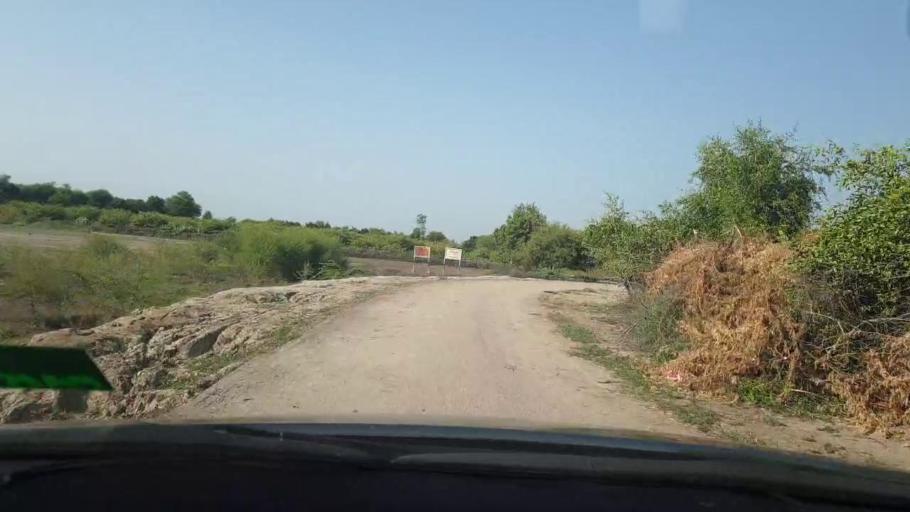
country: PK
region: Sindh
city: Naukot
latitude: 24.8715
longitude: 69.3171
